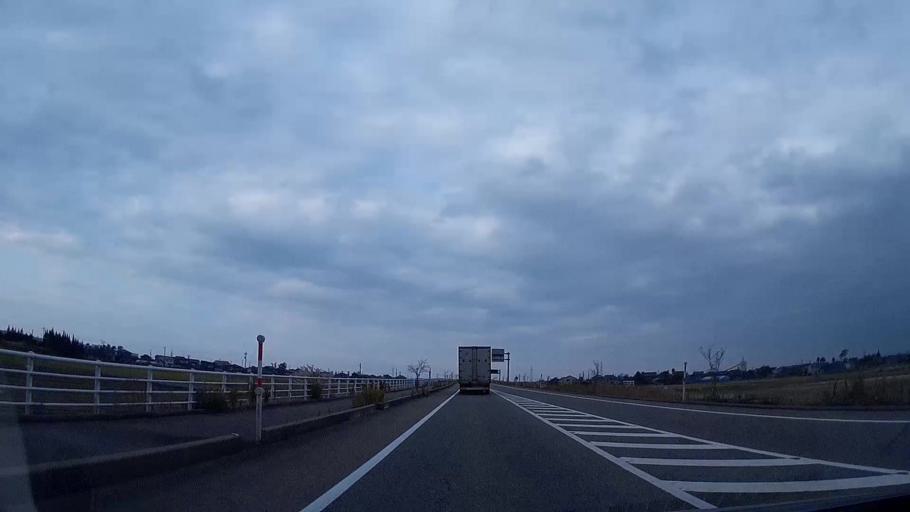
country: JP
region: Toyama
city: Nyuzen
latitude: 36.8938
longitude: 137.4445
